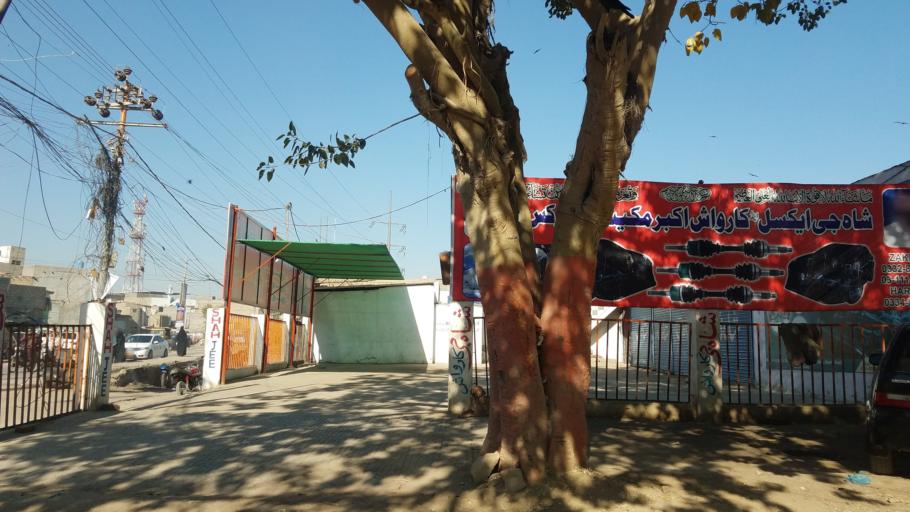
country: PK
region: Sindh
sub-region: Karachi District
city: Karachi
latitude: 24.9230
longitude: 67.0489
